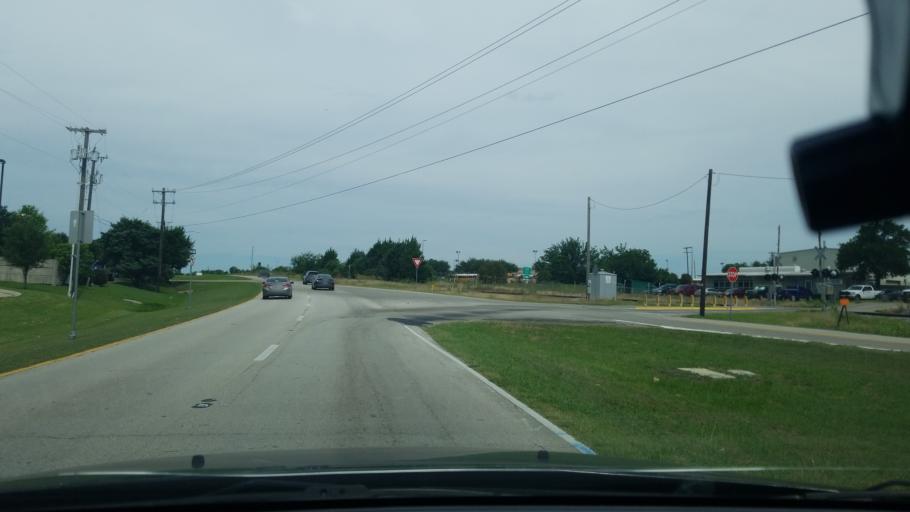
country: US
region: Texas
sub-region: Dallas County
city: Mesquite
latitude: 32.7658
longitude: -96.5859
